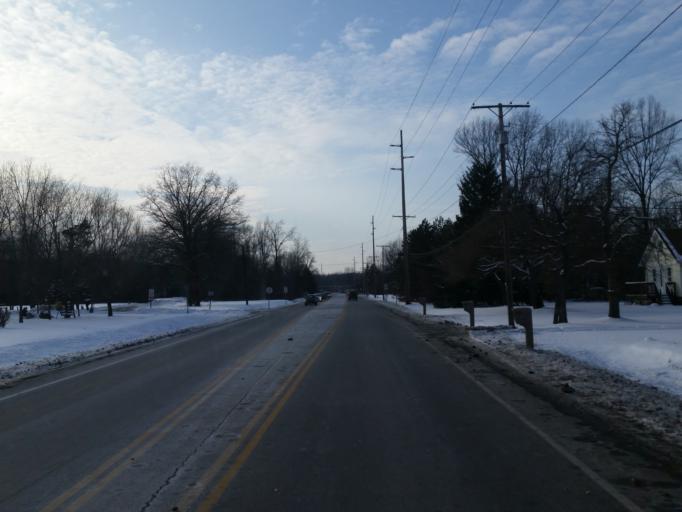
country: US
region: Ohio
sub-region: Lorain County
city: Sheffield Lake
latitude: 41.4653
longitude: -82.0859
